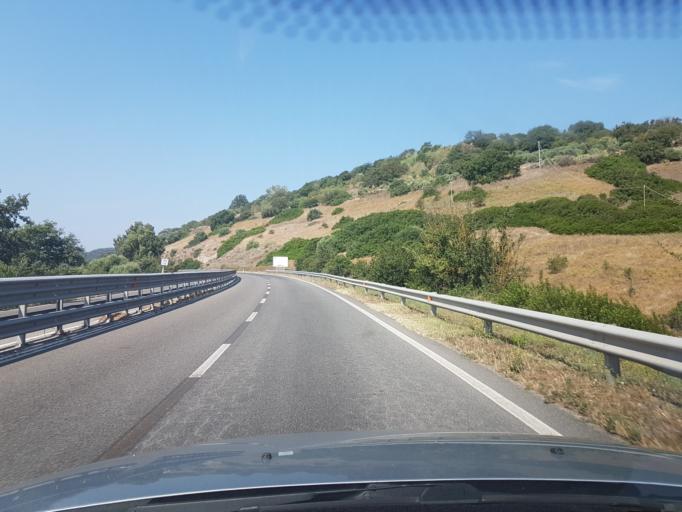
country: IT
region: Sardinia
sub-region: Provincia di Oristano
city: Sedilo
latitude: 40.1636
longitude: 8.9206
